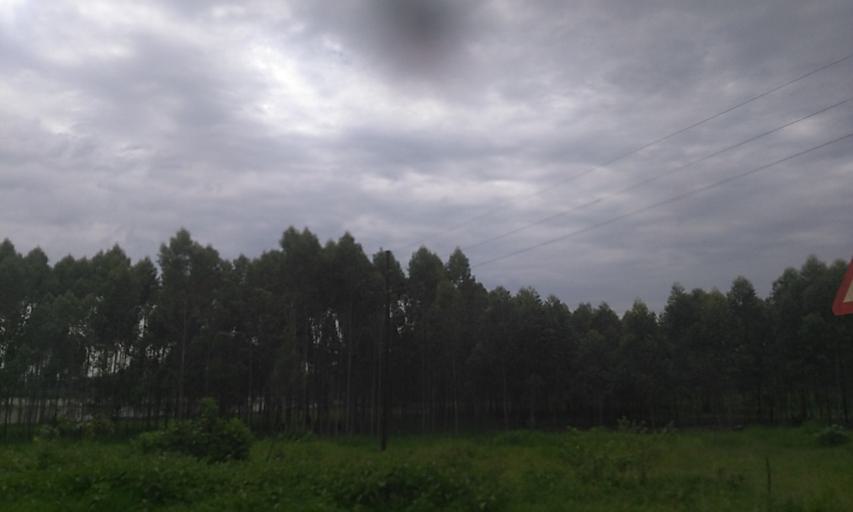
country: UG
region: Central Region
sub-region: Wakiso District
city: Bweyogerere
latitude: 0.3971
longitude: 32.6755
